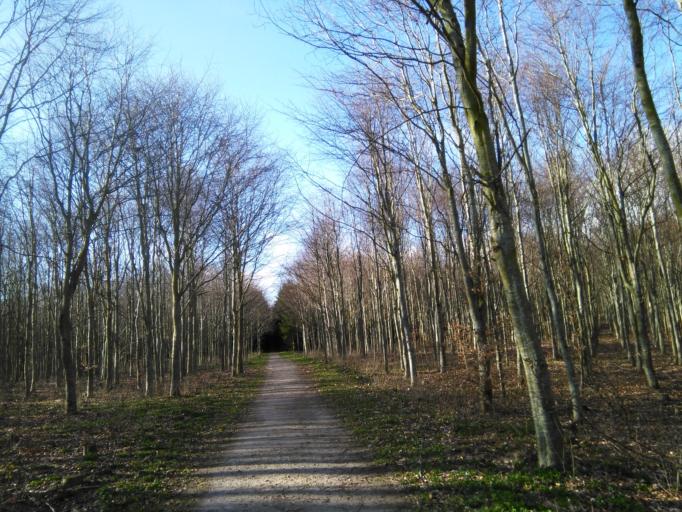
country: DK
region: Central Jutland
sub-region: Arhus Kommune
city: Beder
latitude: 56.0644
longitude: 10.2060
